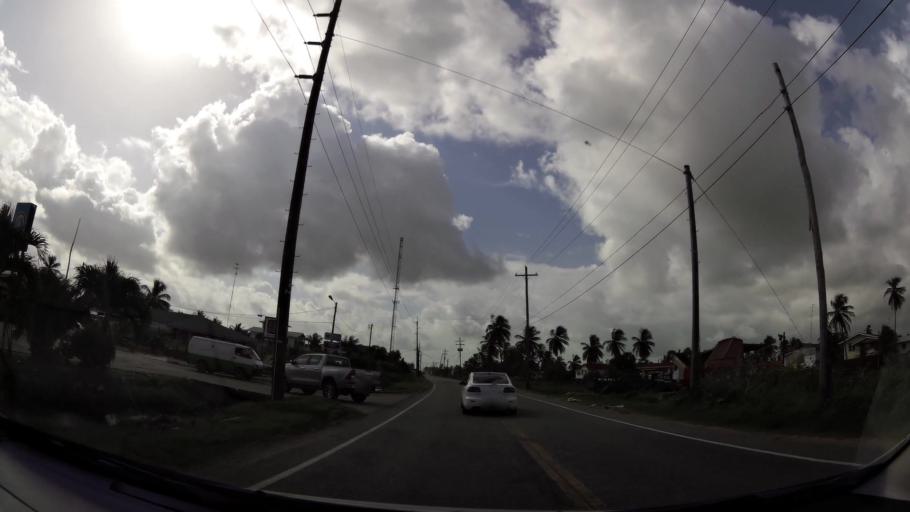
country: GY
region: Demerara-Mahaica
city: Mahaica Village
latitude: 6.6789
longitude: -57.9245
